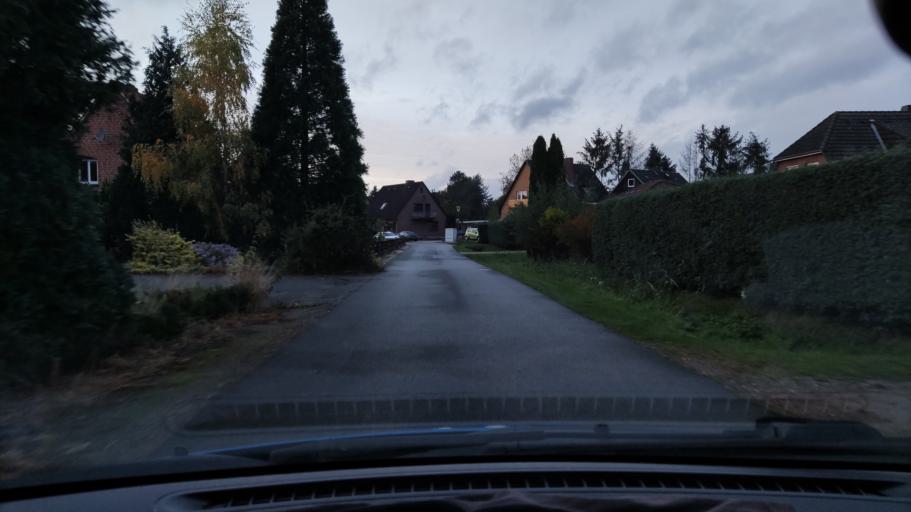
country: DE
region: Lower Saxony
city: Artlenburg
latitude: 53.3670
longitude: 10.4803
